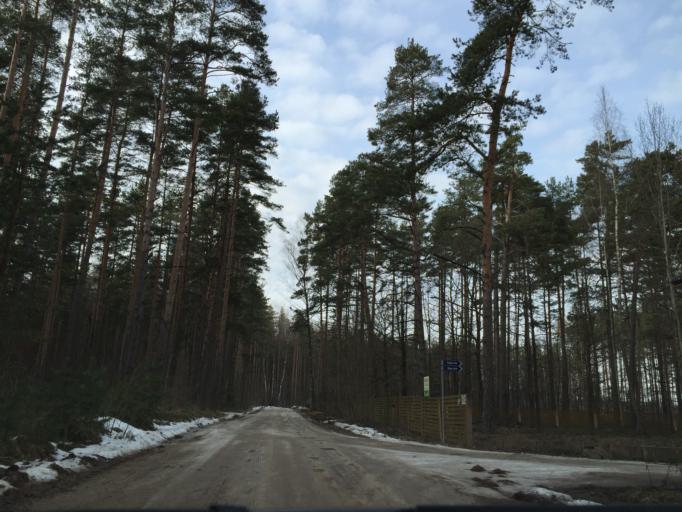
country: LV
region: Stopini
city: Ulbroka
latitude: 56.9236
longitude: 24.2866
